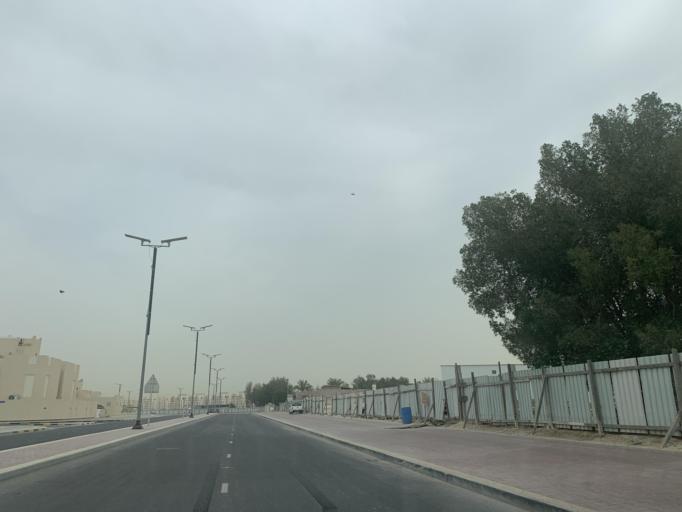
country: BH
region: Northern
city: Madinat `Isa
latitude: 26.1679
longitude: 50.5101
